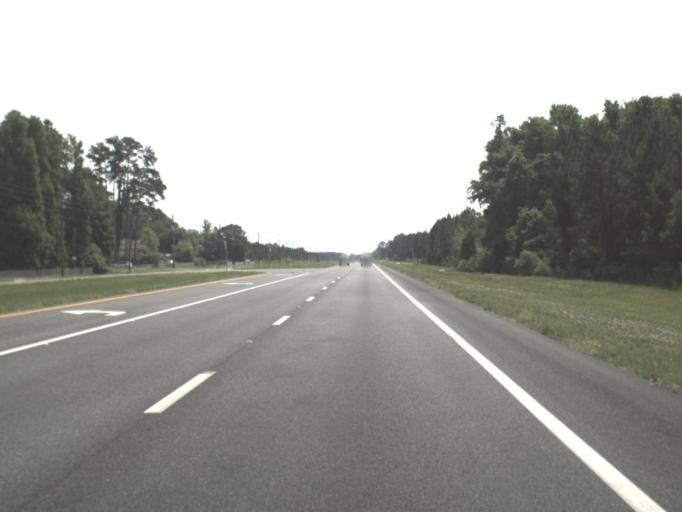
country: US
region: Florida
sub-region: Nassau County
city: Callahan
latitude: 30.5935
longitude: -81.7778
